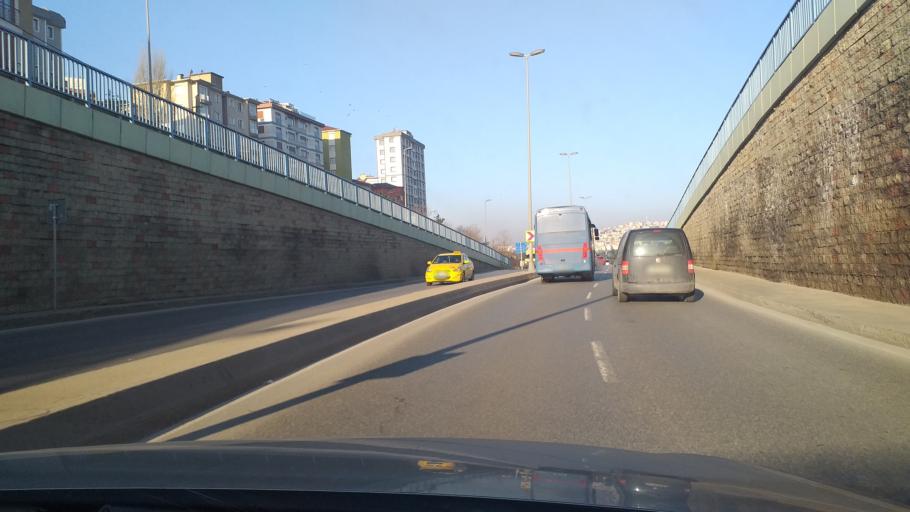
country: TR
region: Istanbul
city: Maltepe
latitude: 40.9207
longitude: 29.1938
